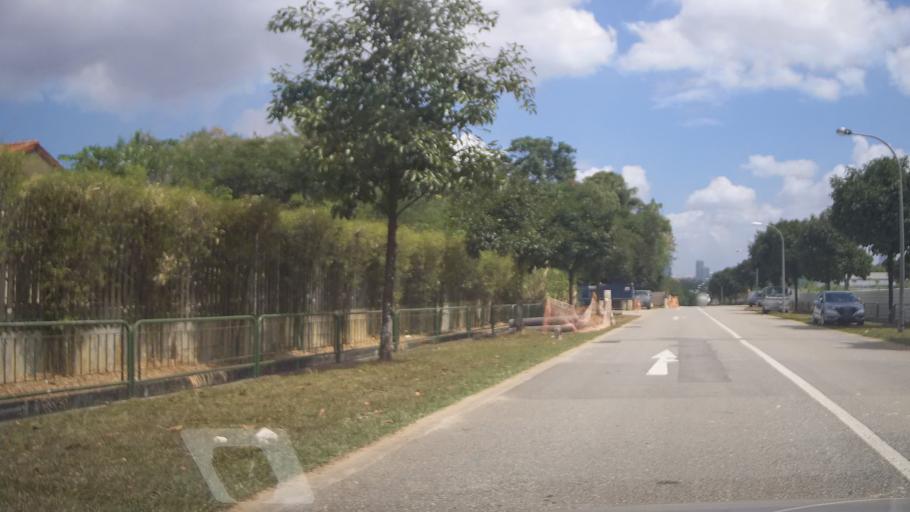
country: MY
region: Johor
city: Johor Bahru
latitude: 1.4373
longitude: 103.7257
